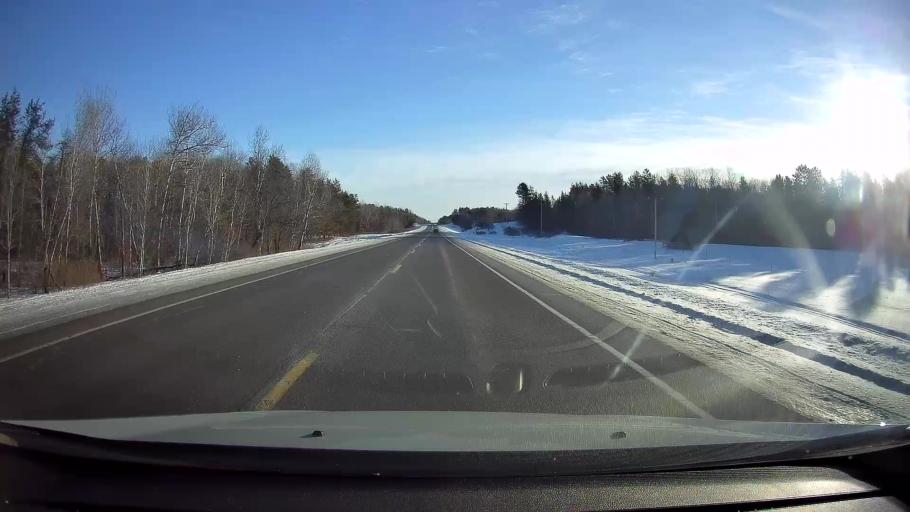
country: US
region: Wisconsin
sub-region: Washburn County
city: Spooner
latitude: 45.9104
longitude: -91.7949
